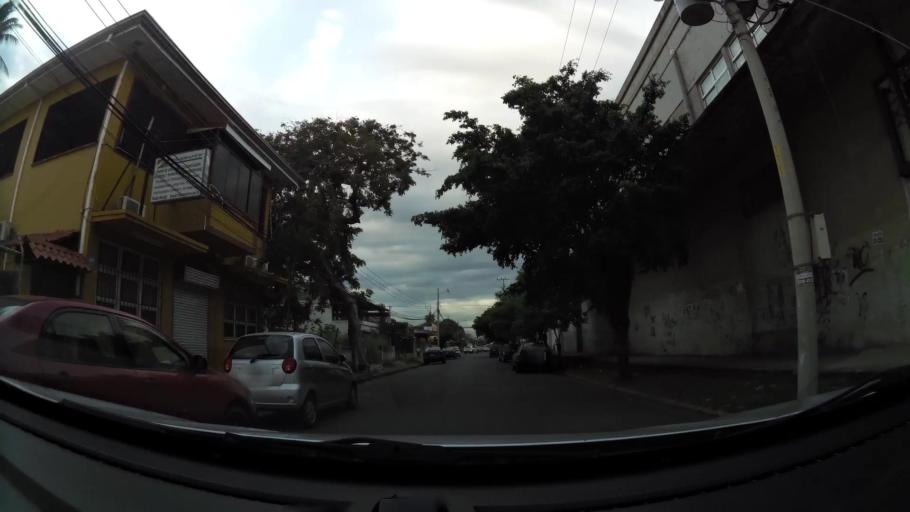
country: CR
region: Puntarenas
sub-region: Canton Central de Puntarenas
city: Puntarenas
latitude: 9.9756
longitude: -84.8335
